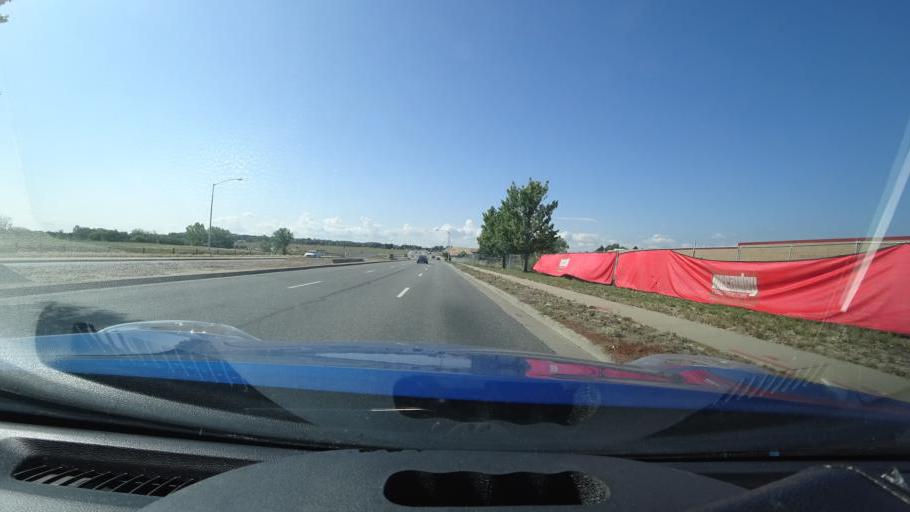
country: US
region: Colorado
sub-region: Adams County
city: Aurora
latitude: 39.7128
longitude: -104.7913
